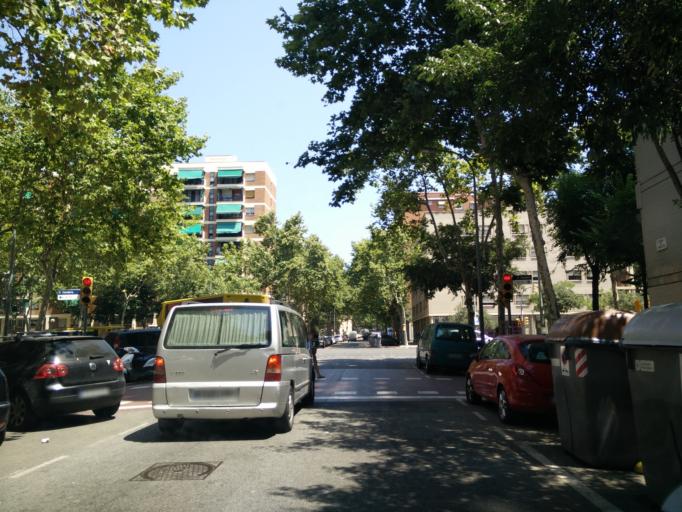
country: ES
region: Catalonia
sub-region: Provincia de Barcelona
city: Sant Marti
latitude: 41.4202
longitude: 2.1999
